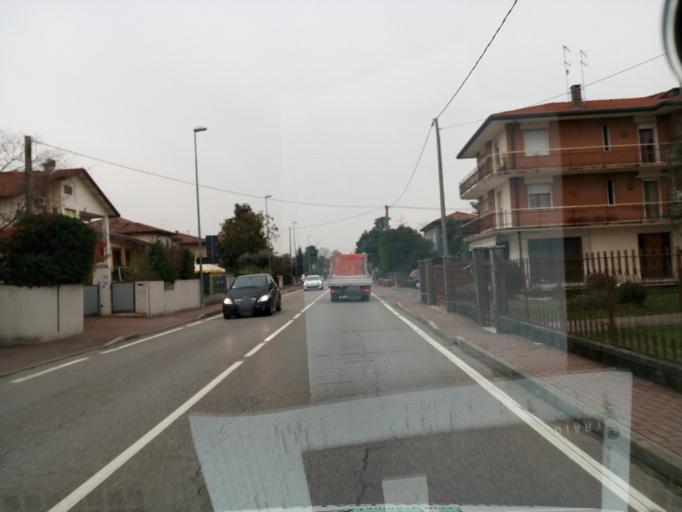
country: IT
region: Veneto
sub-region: Provincia di Padova
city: Piombino Dese
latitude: 45.6063
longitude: 12.0024
